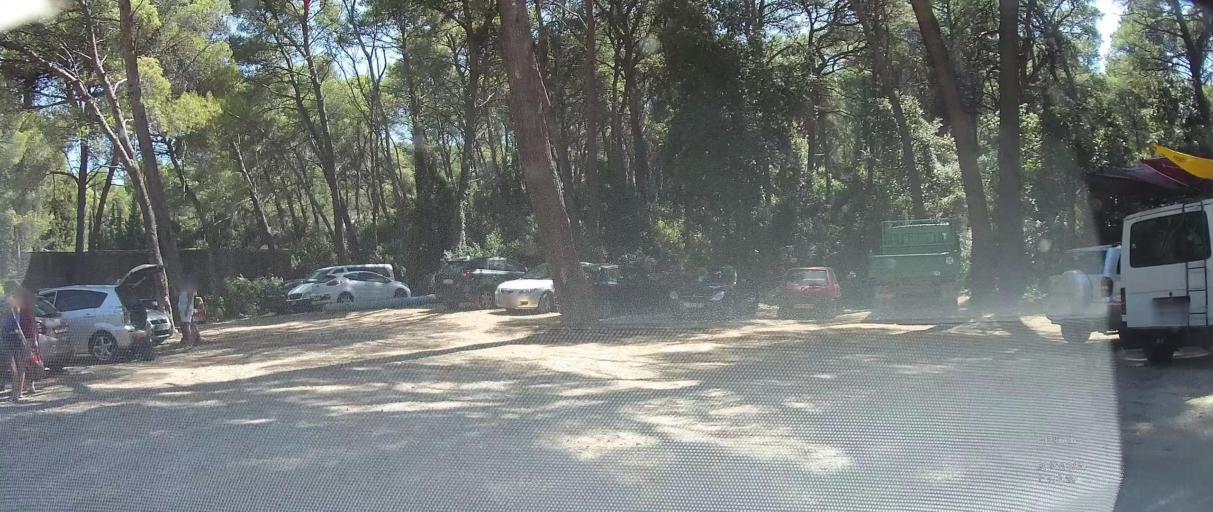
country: HR
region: Dubrovacko-Neretvanska
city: Blato
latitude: 42.7784
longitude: 17.3685
